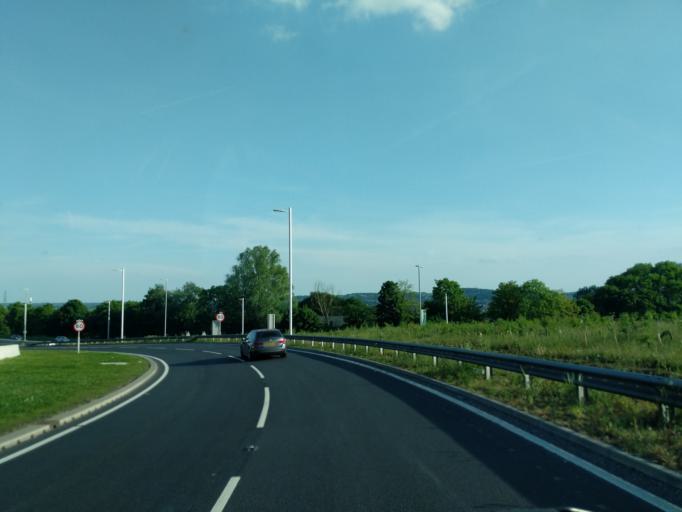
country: GB
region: England
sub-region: Borough of Halton
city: Halton
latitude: 53.3190
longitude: -2.7152
